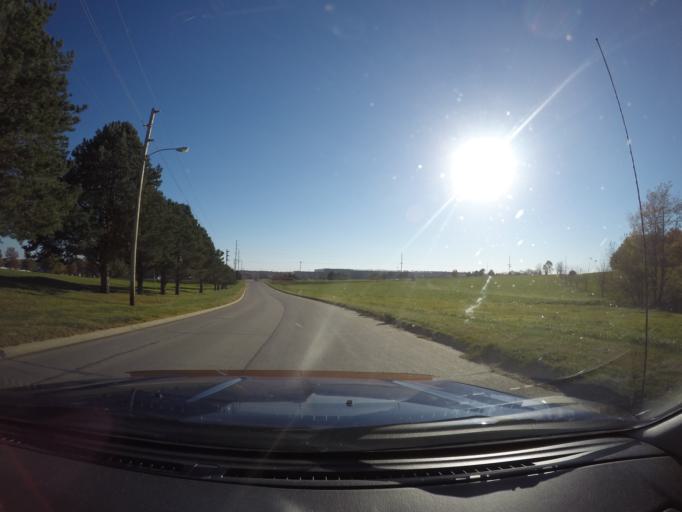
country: US
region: Nebraska
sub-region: Otoe County
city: Nebraska City
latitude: 40.6693
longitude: -95.8782
